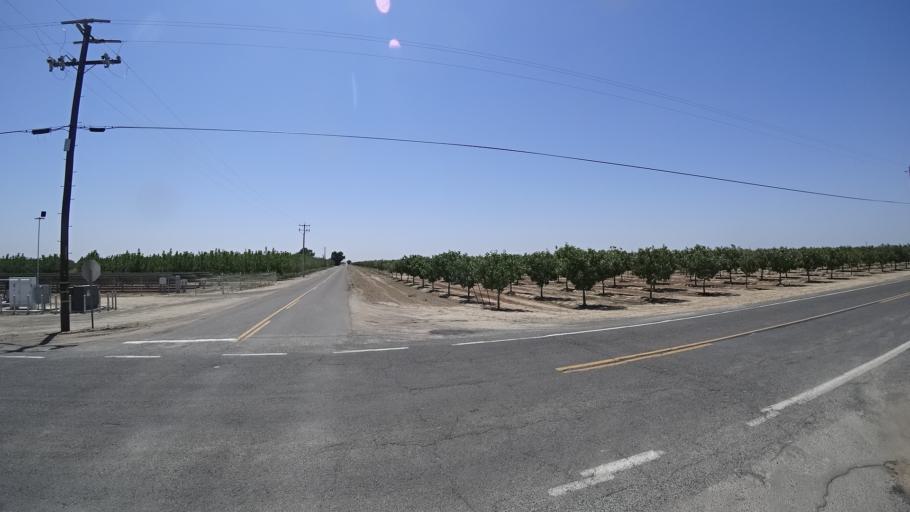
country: US
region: California
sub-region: Kings County
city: Armona
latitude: 36.2547
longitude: -119.7269
